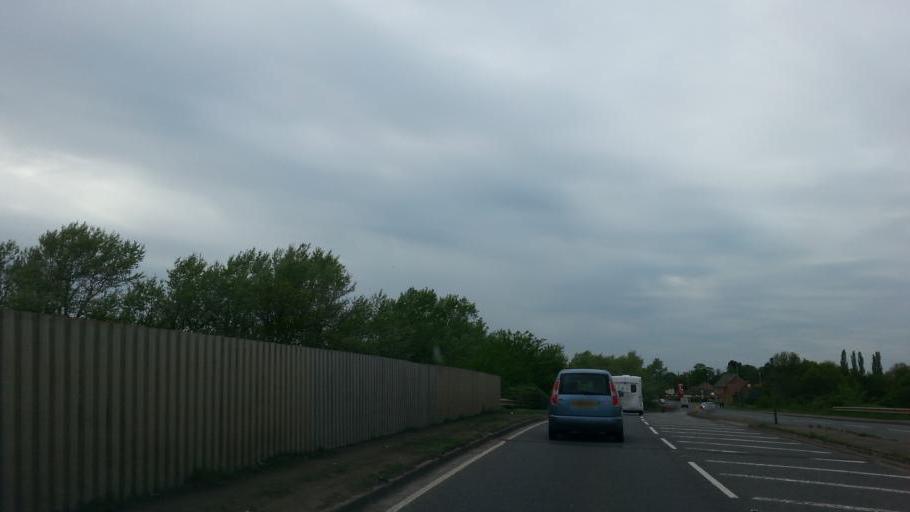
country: GB
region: England
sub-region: Cambridgeshire
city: March
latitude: 52.5598
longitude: 0.0663
